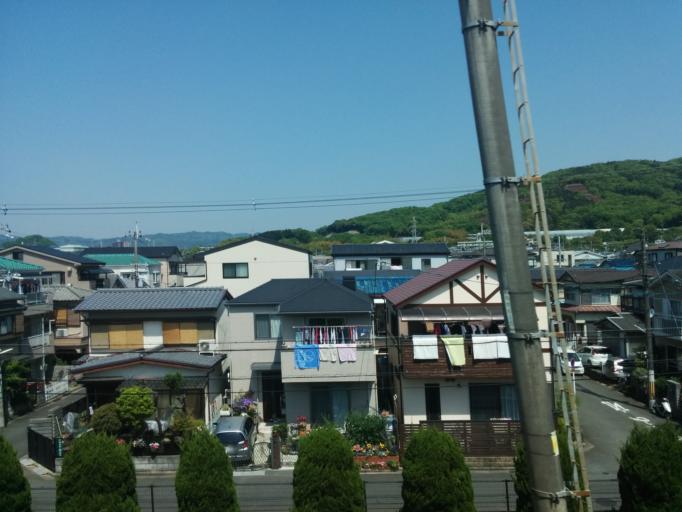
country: JP
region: Osaka
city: Takatsuki
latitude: 34.8576
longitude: 135.6393
